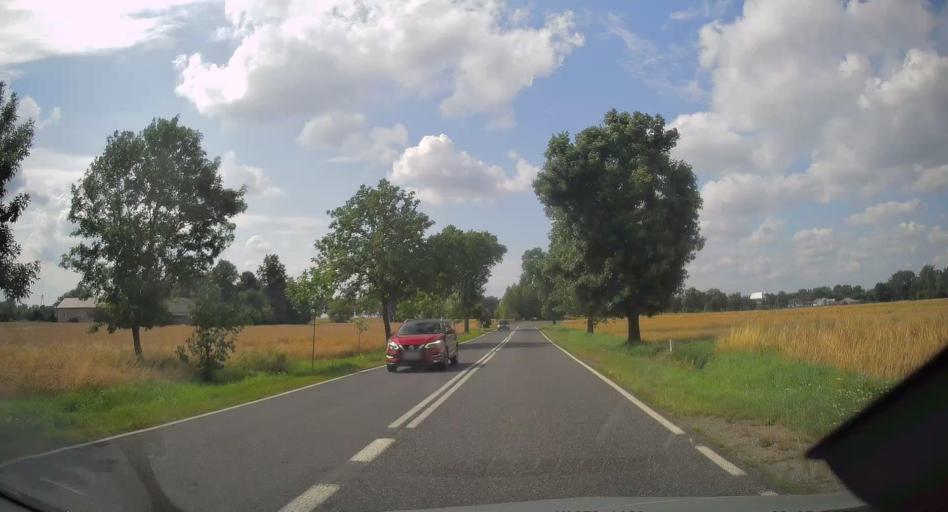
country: PL
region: Lodz Voivodeship
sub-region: Powiat brzezinski
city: Jezow
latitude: 51.8026
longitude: 20.0175
